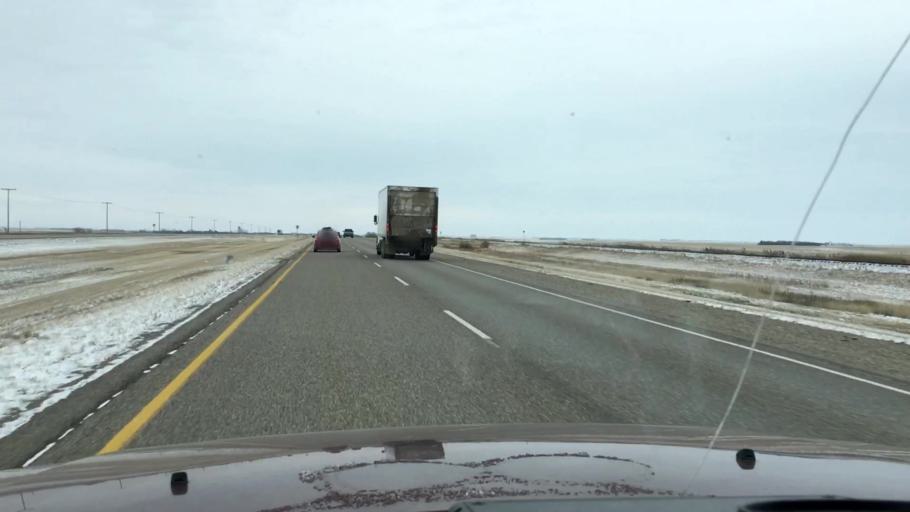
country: CA
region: Saskatchewan
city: Watrous
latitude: 51.1814
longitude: -105.9402
